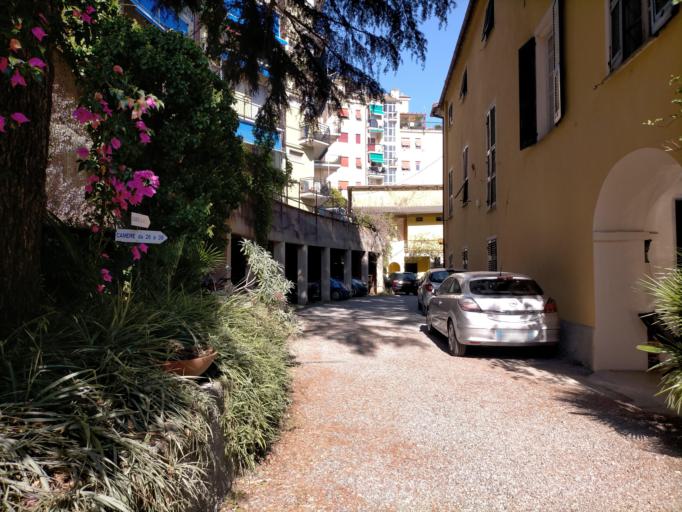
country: IT
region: Liguria
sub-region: Provincia di Genova
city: Cogoleto
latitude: 44.3908
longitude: 8.6489
